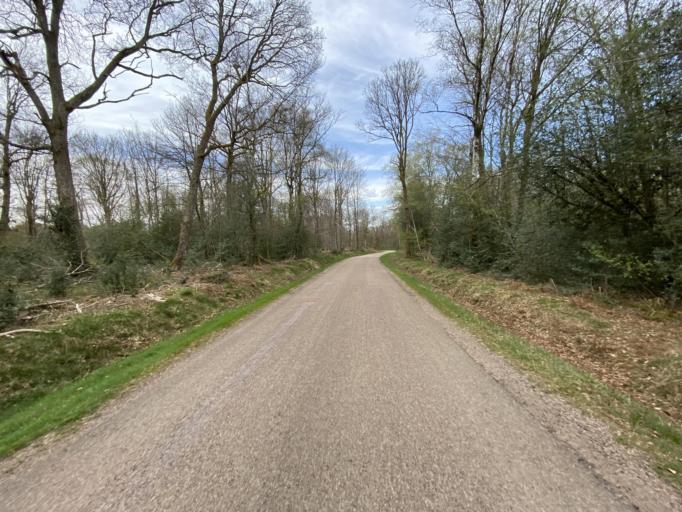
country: FR
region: Bourgogne
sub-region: Departement de la Cote-d'Or
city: Saulieu
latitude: 47.2998
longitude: 4.0881
